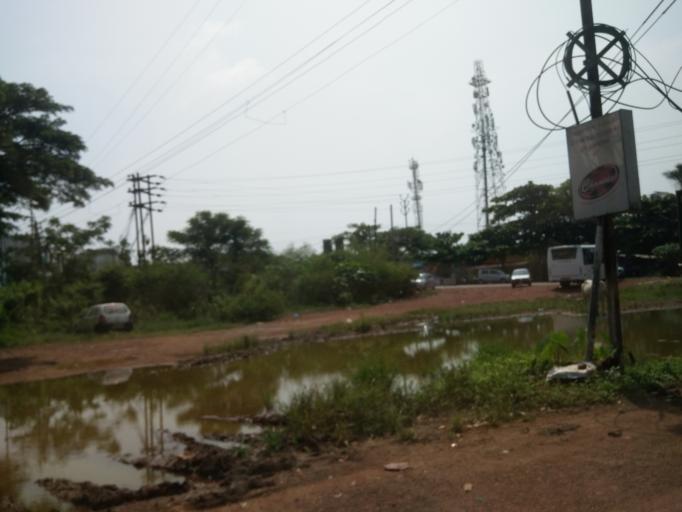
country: IN
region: Goa
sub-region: North Goa
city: Bambolim
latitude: 15.4646
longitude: 73.8565
